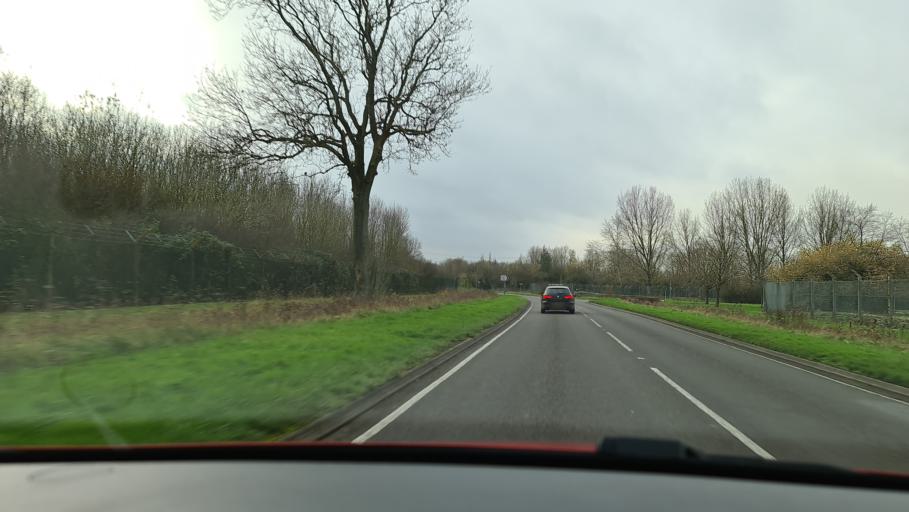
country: GB
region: England
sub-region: Oxfordshire
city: Bicester
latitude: 51.8542
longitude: -1.0902
